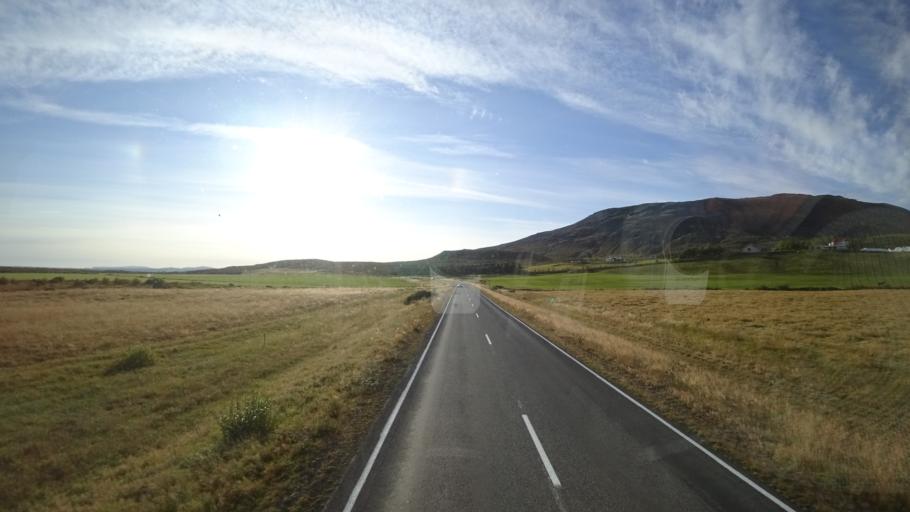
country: IS
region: South
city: Selfoss
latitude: 64.2398
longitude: -20.5418
